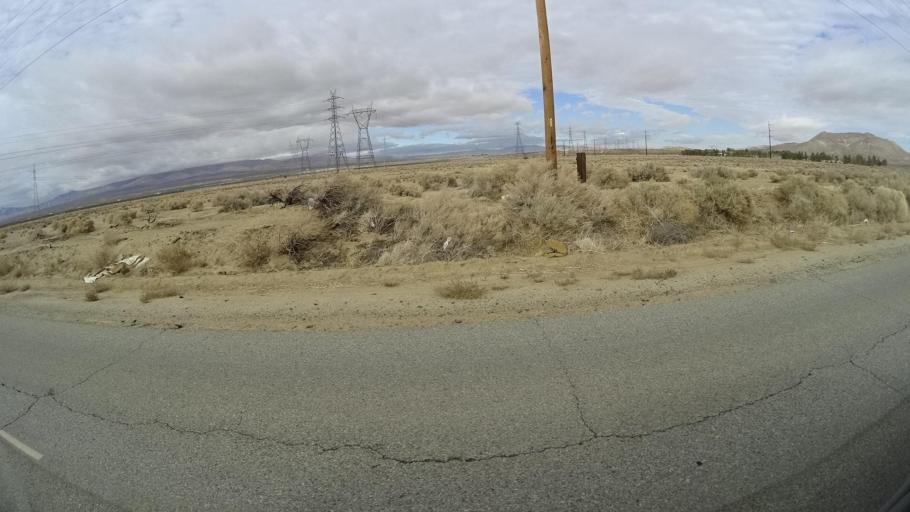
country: US
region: California
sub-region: Kern County
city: Rosamond
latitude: 34.8631
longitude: -118.3122
